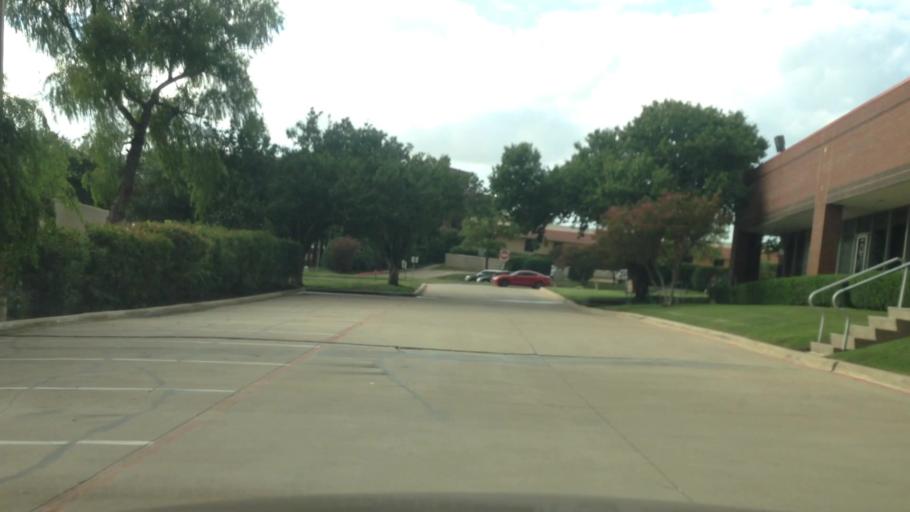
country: US
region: Texas
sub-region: Dallas County
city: Irving
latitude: 32.8839
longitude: -96.9731
